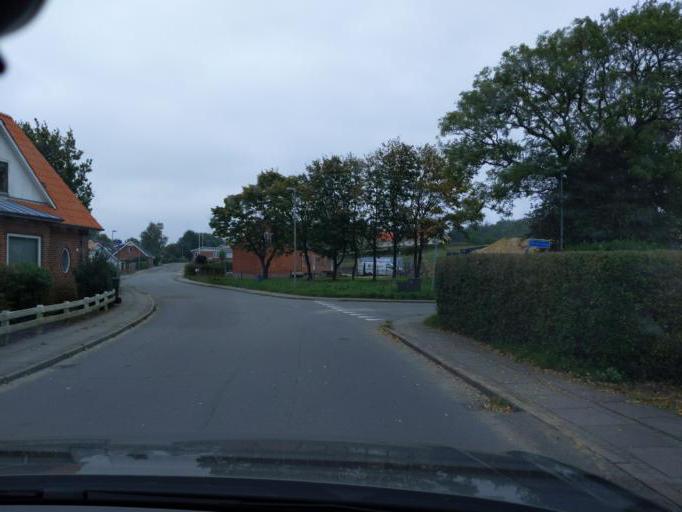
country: DK
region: Central Jutland
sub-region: Viborg Kommune
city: Stoholm
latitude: 56.4781
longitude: 9.2295
